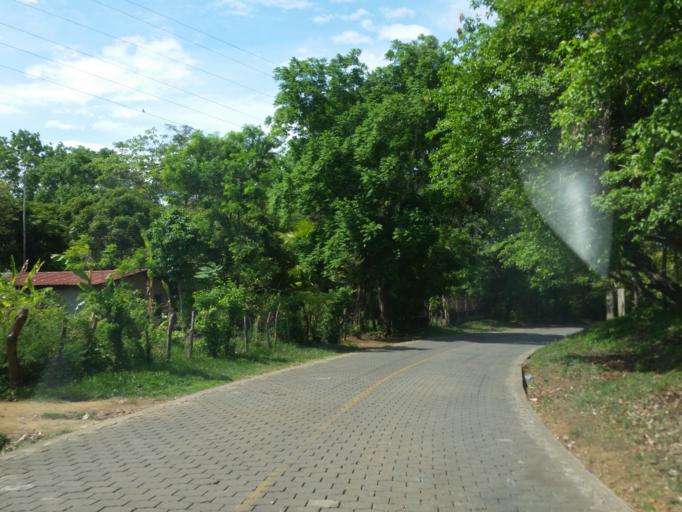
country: NI
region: Masaya
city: Masaya
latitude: 11.9686
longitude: -86.0311
